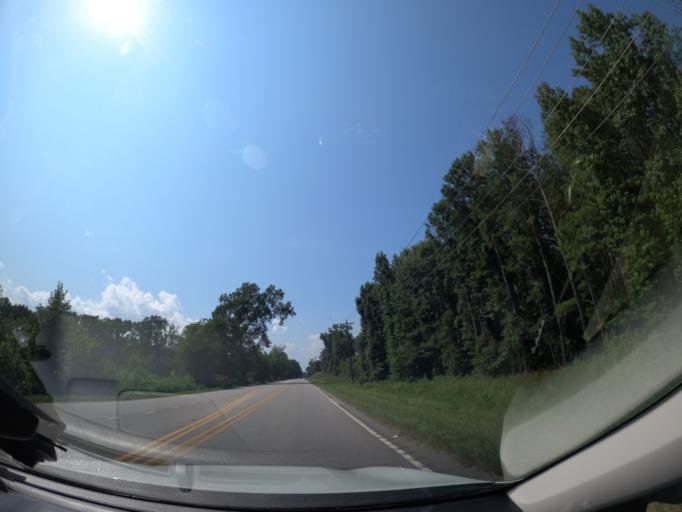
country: US
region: South Carolina
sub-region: Richland County
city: Hopkins
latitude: 33.9203
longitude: -80.9531
